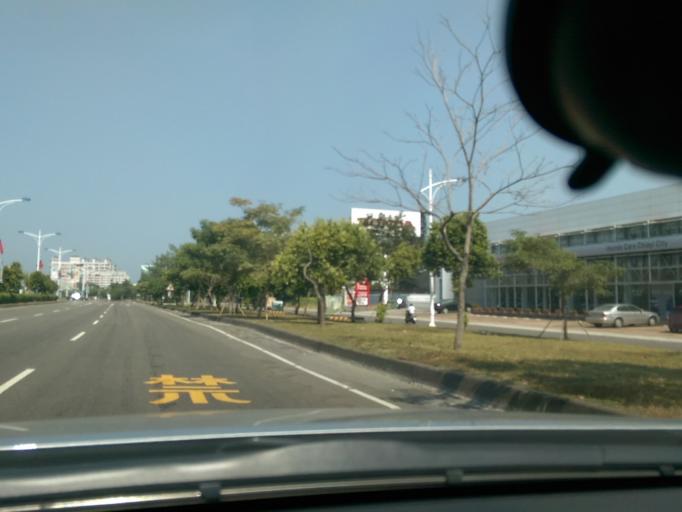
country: TW
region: Taiwan
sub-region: Chiayi
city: Jiayi Shi
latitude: 23.5075
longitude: 120.4469
